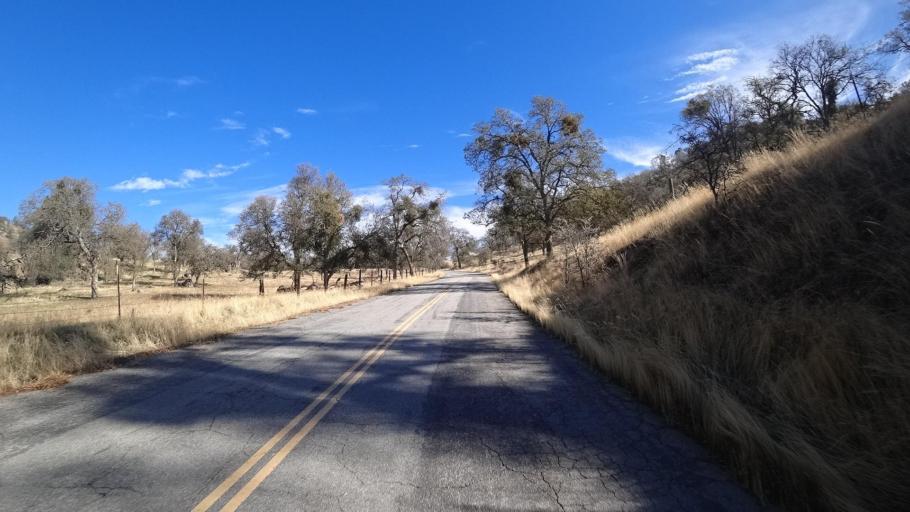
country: US
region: California
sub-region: Kern County
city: Alta Sierra
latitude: 35.6304
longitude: -118.7817
